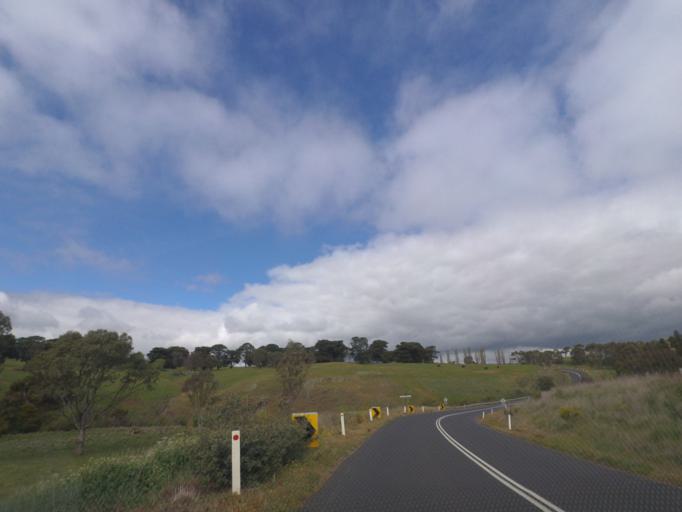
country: AU
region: Victoria
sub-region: Hume
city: Sunbury
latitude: -37.3467
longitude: 144.7808
